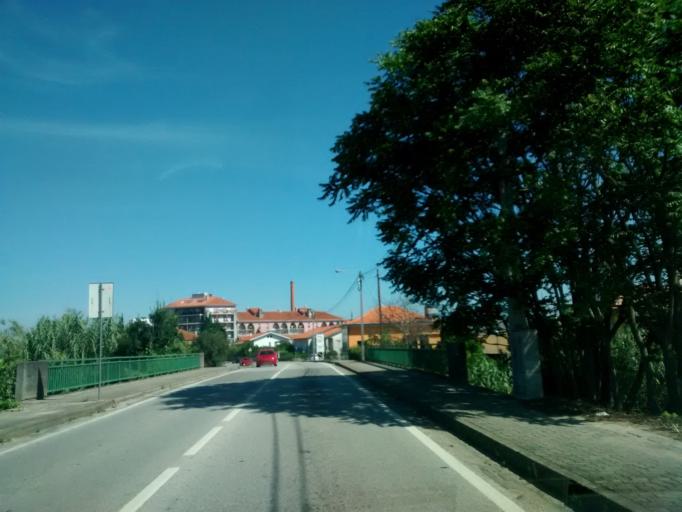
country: PT
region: Aveiro
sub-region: Anadia
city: Arcos
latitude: 40.4488
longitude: -8.4514
